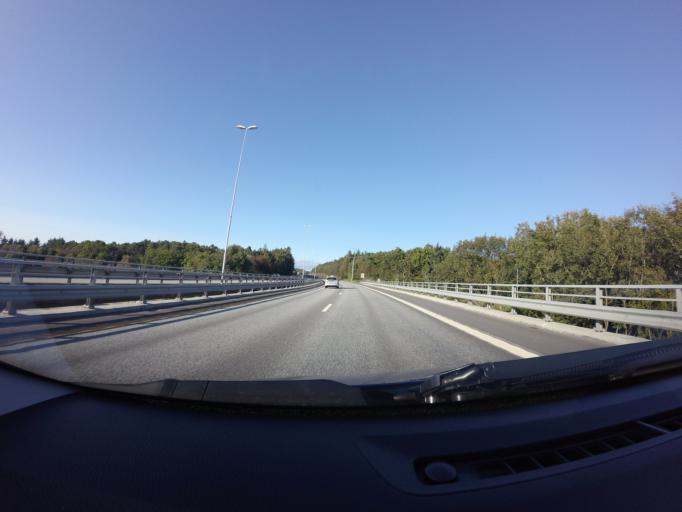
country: NO
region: Rogaland
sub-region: Stavanger
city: Stavanger
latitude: 58.9228
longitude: 5.7071
